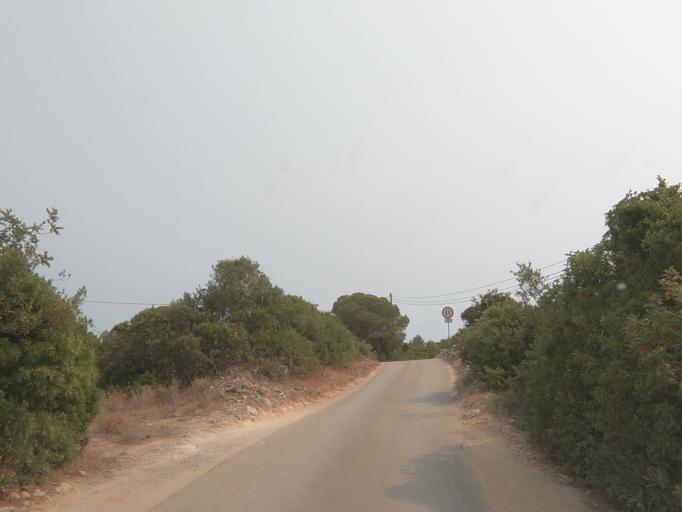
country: PT
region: Faro
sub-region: Silves
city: Armacao de Pera
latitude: 37.0954
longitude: -8.4029
